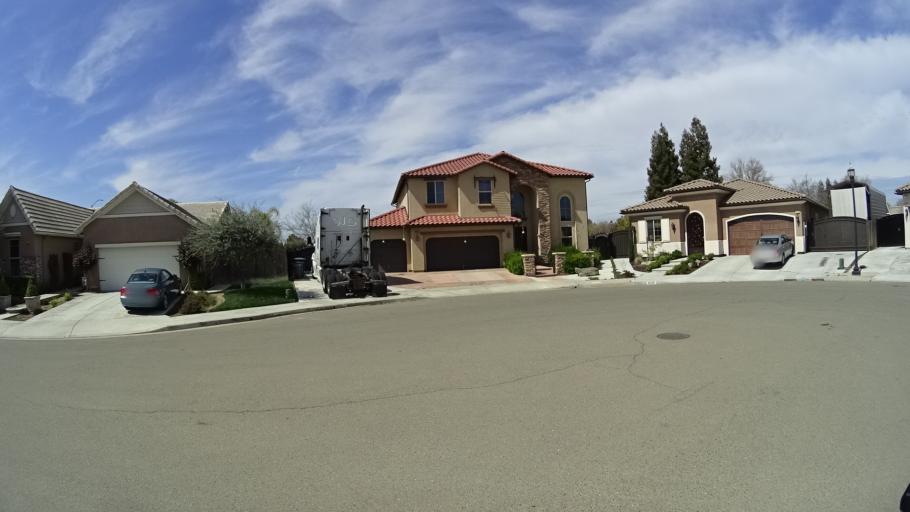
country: US
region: California
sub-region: Fresno County
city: Biola
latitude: 36.8253
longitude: -119.9158
